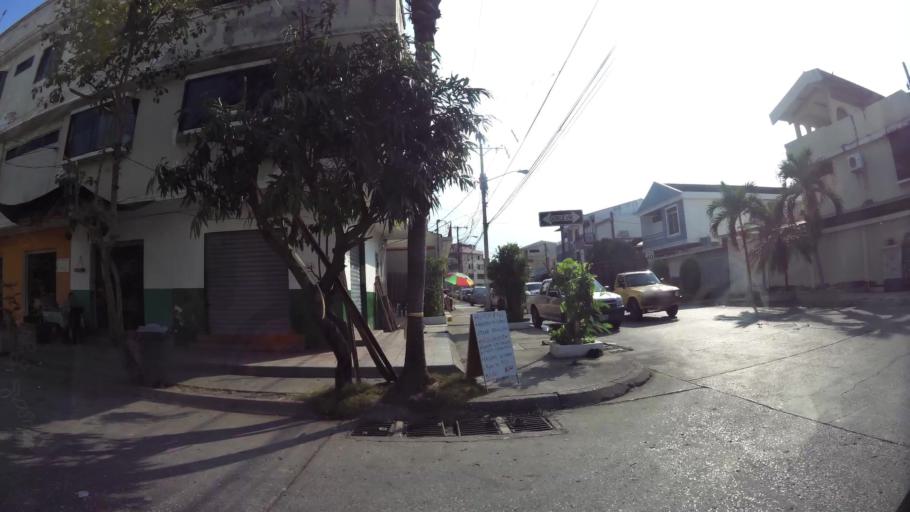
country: EC
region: Guayas
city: Guayaquil
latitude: -2.1495
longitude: -79.9082
